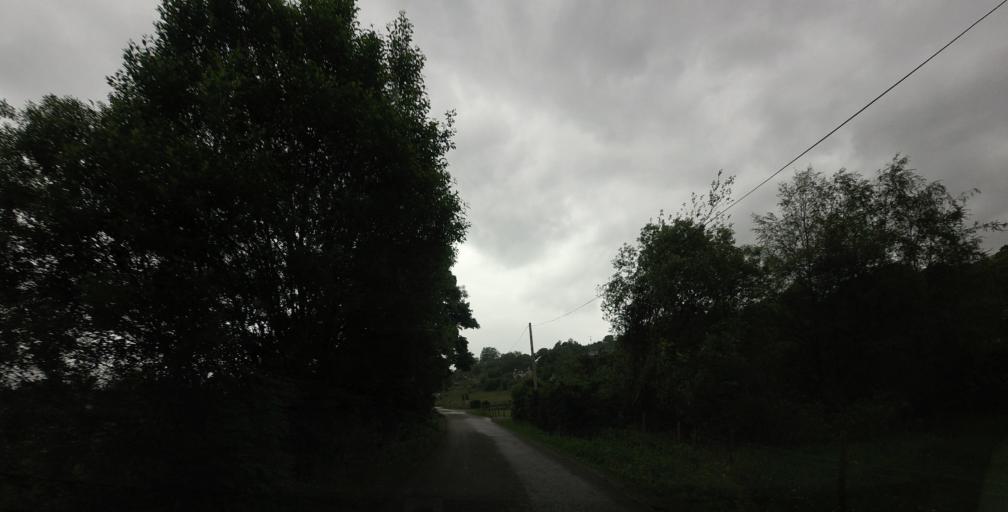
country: GB
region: Scotland
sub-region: Argyll and Bute
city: Oban
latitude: 56.7054
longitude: -5.5690
